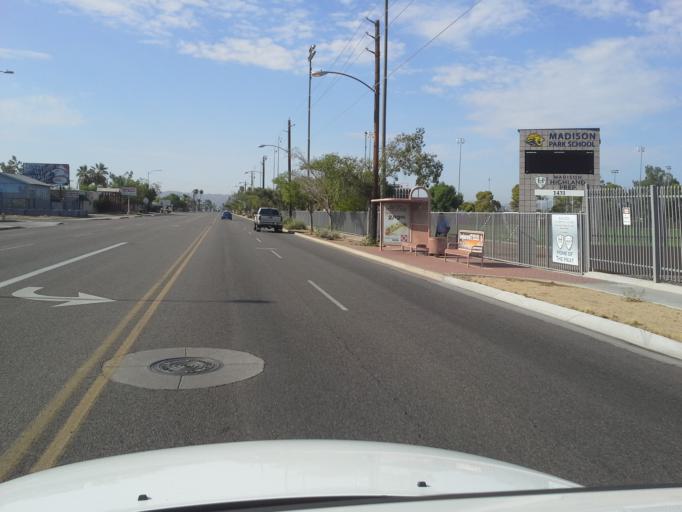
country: US
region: Arizona
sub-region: Maricopa County
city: Phoenix
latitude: 33.5018
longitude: -112.0476
